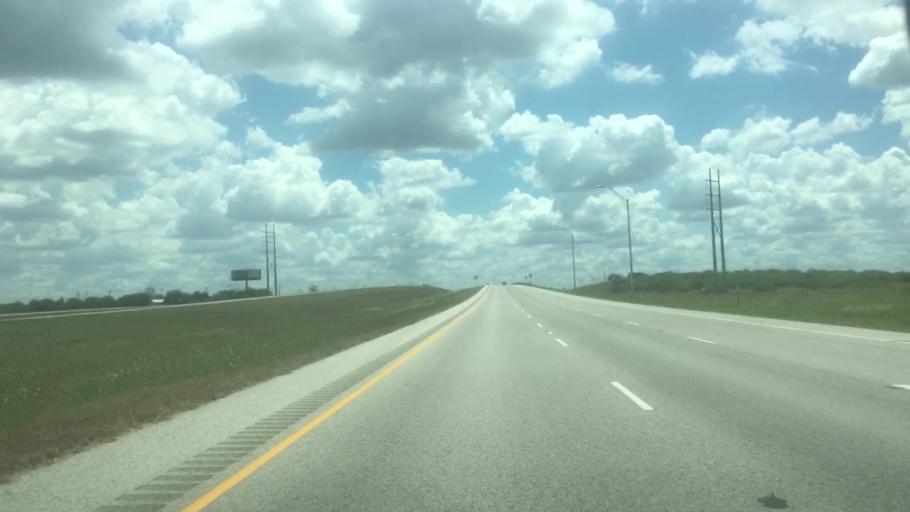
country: US
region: Texas
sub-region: Caldwell County
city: Uhland
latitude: 30.0106
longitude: -97.6880
